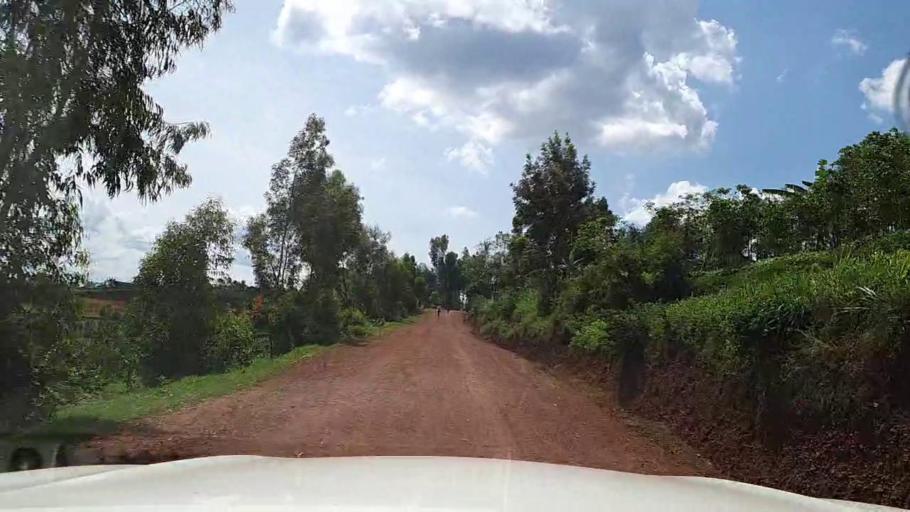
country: RW
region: Southern Province
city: Butare
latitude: -2.7443
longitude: 29.6983
